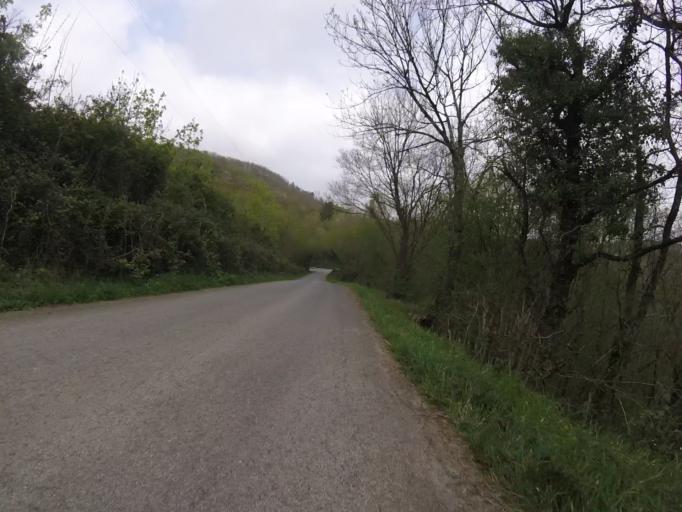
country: ES
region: Basque Country
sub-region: Provincia de Guipuzcoa
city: Asteasu
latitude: 43.2190
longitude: -2.0922
